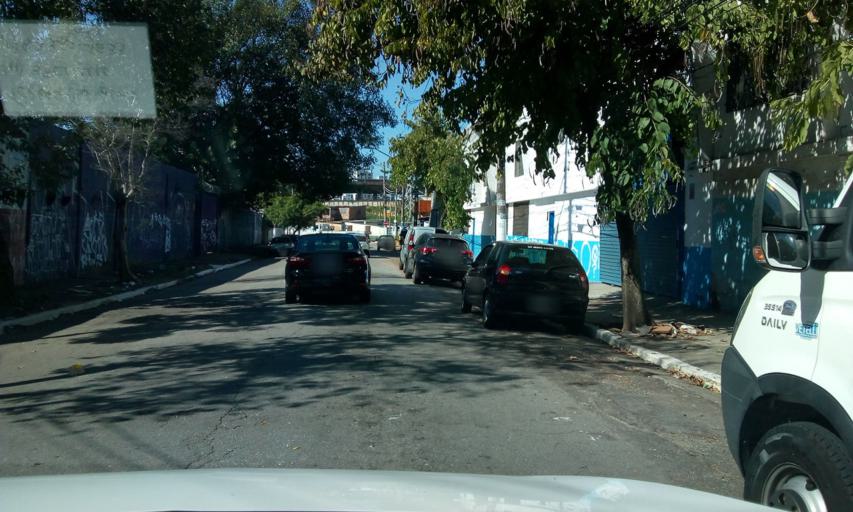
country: BR
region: Sao Paulo
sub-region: Guarulhos
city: Guarulhos
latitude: -23.5330
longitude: -46.5549
